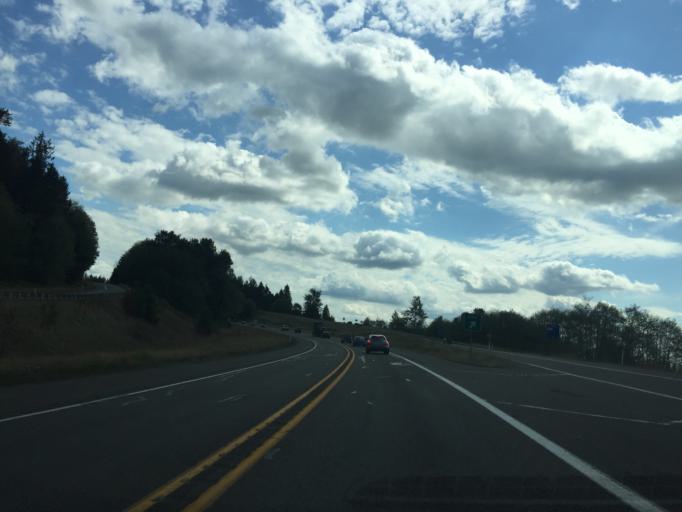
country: US
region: Washington
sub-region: Snohomish County
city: Snohomish
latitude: 47.9187
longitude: -122.0748
